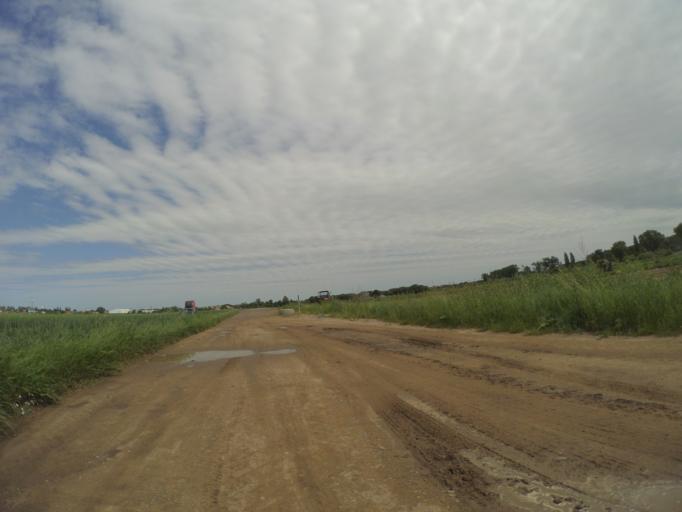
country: CZ
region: Central Bohemia
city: Lysa nad Labem
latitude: 50.1843
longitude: 14.8376
